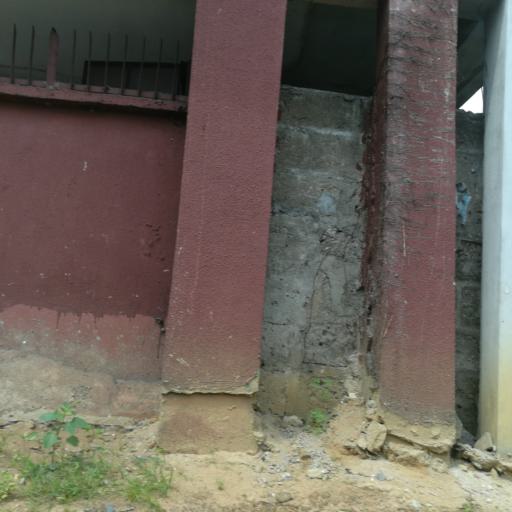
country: NG
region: Rivers
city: Port Harcourt
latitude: 4.7929
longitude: 7.0280
